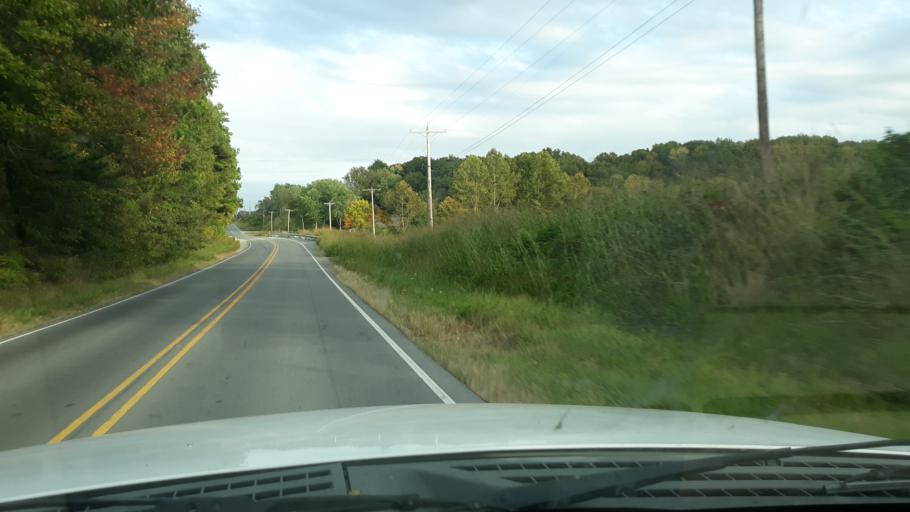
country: US
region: Illinois
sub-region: Saline County
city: Eldorado
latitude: 37.8225
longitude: -88.4972
